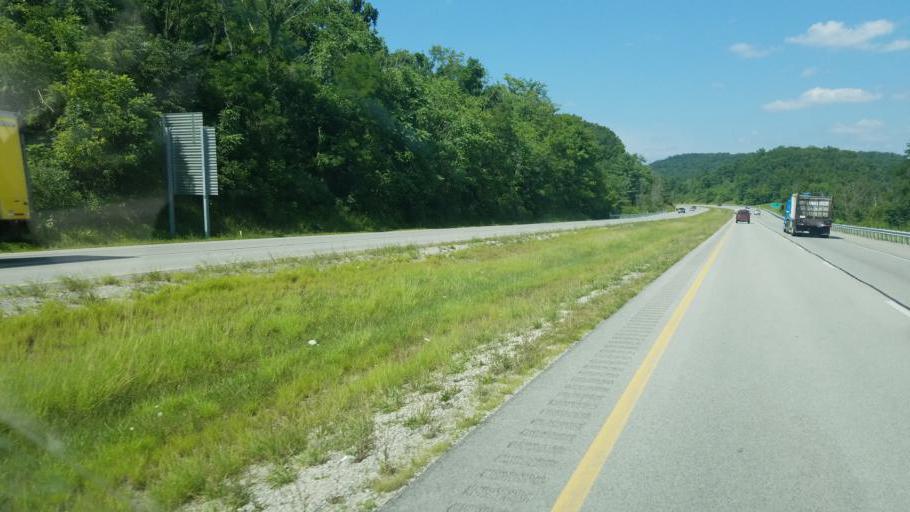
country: US
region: West Virginia
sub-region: Kanawha County
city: Sissonville
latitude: 38.6759
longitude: -81.6435
